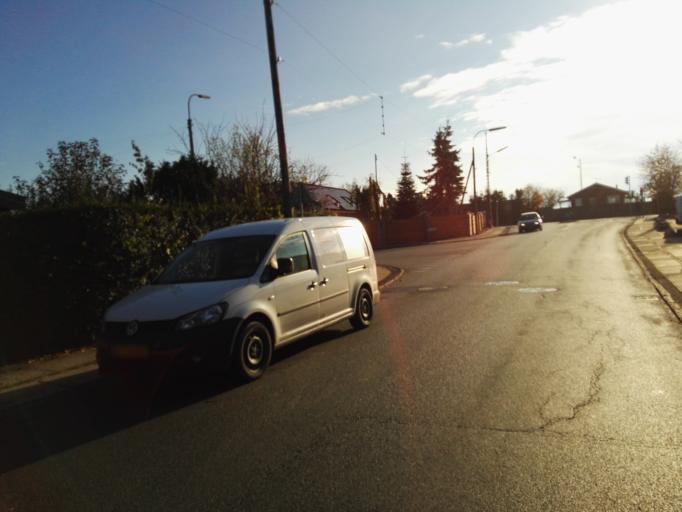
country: DK
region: Capital Region
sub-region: Herlev Kommune
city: Herlev
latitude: 55.7268
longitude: 12.4119
